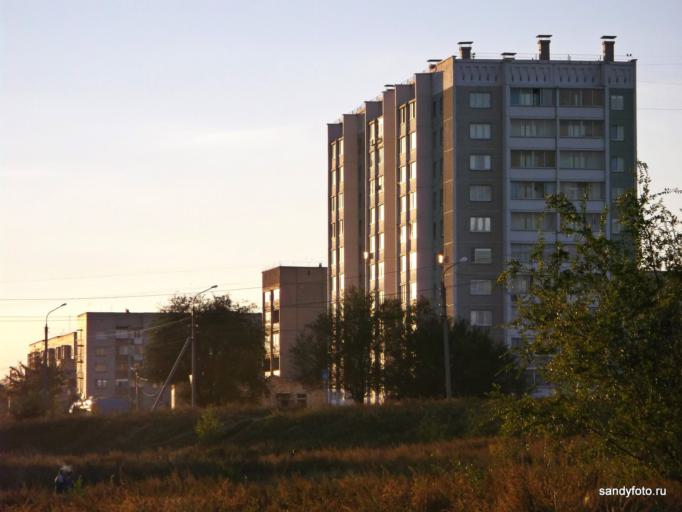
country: RU
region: Chelyabinsk
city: Troitsk
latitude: 54.0755
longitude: 61.5321
